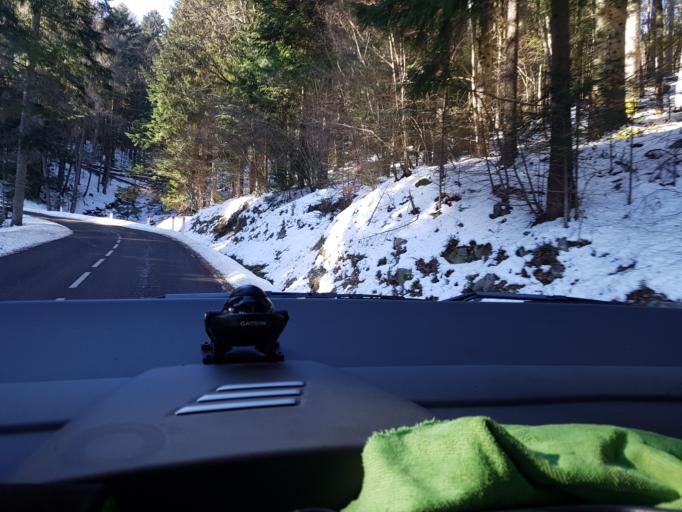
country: FR
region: Alsace
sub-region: Departement du Haut-Rhin
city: Metzeral
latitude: 47.9898
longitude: 7.0585
